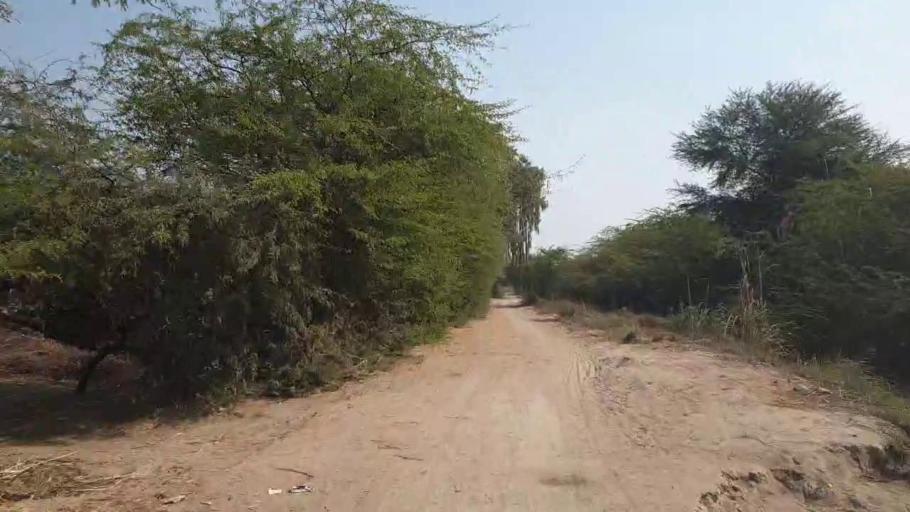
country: PK
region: Sindh
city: Chambar
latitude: 25.4077
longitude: 68.9090
